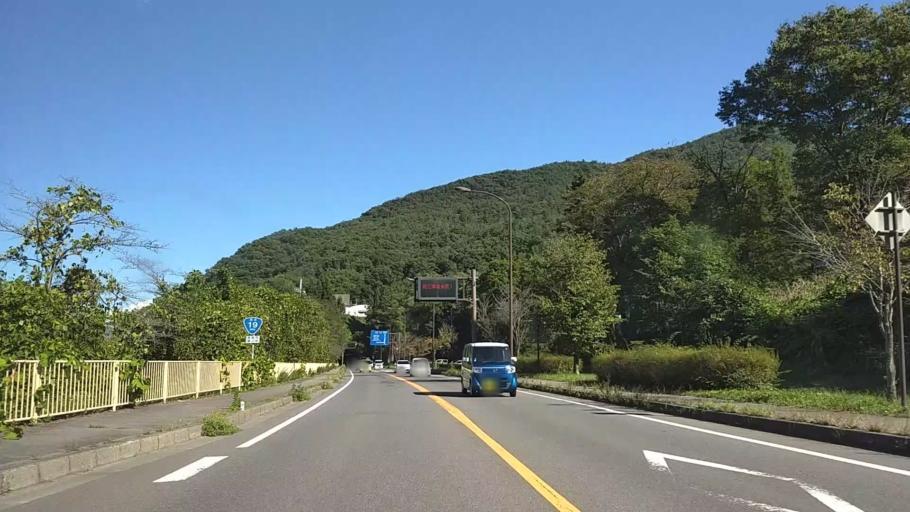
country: JP
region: Nagano
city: Nagano-shi
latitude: 36.6207
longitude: 138.1076
